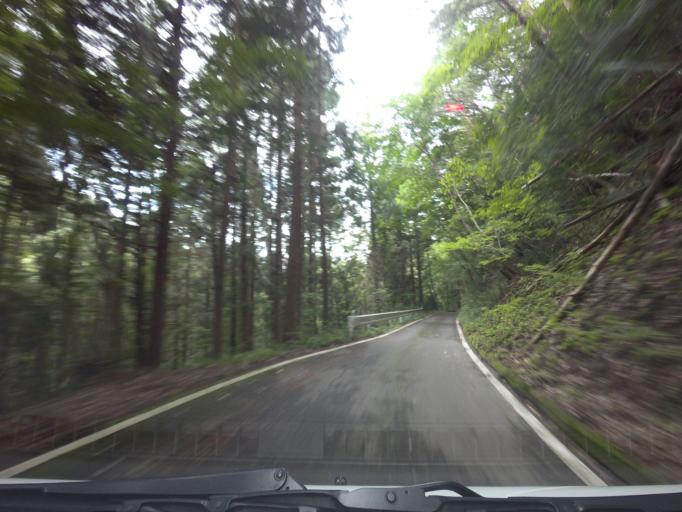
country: JP
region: Fukushima
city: Motomiya
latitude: 37.5491
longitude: 140.3019
